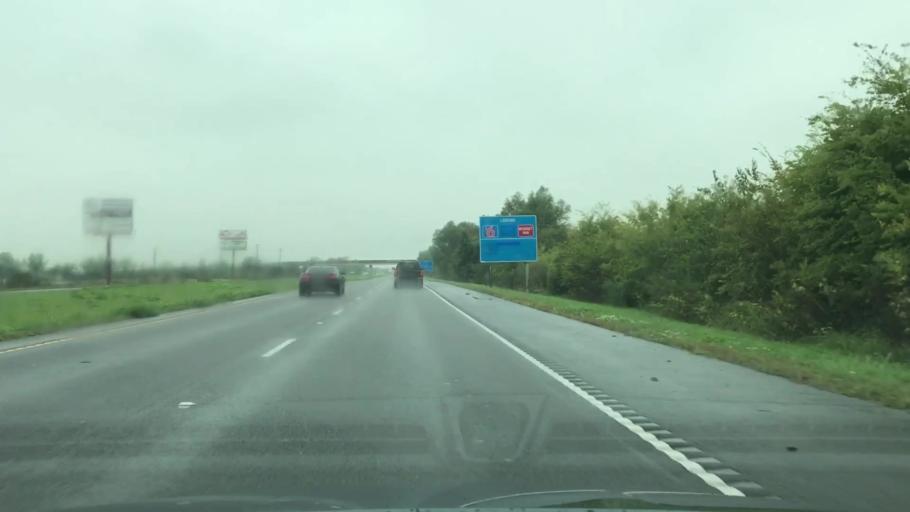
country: US
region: Louisiana
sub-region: Lafourche Parish
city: Raceland
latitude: 29.6898
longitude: -90.6178
